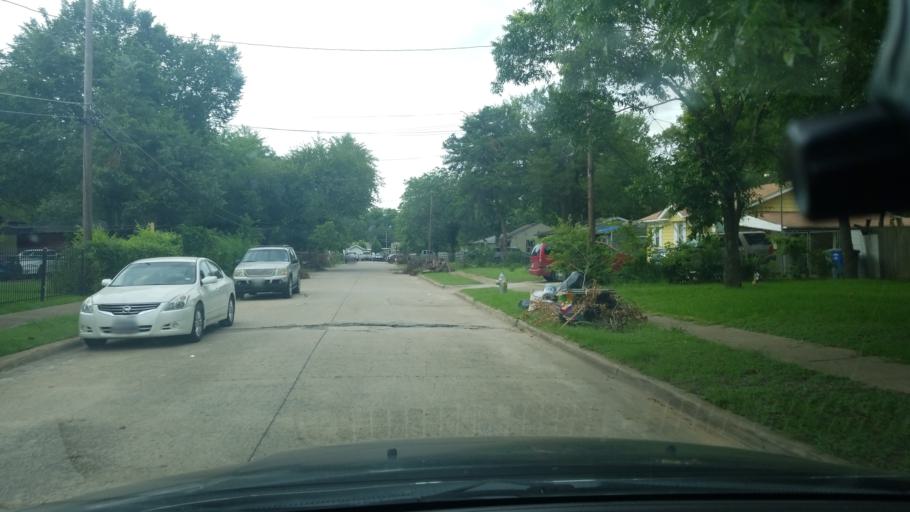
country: US
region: Texas
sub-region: Dallas County
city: Balch Springs
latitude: 32.7332
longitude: -96.6700
